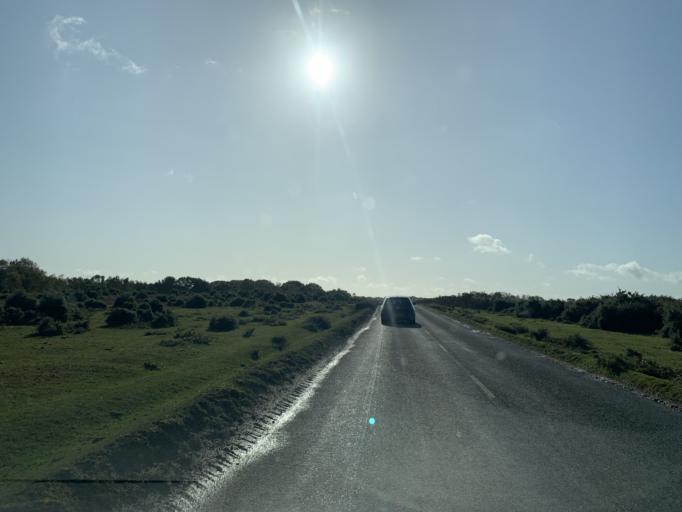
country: GB
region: England
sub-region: Wiltshire
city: Downton
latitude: 50.9584
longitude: -1.6962
